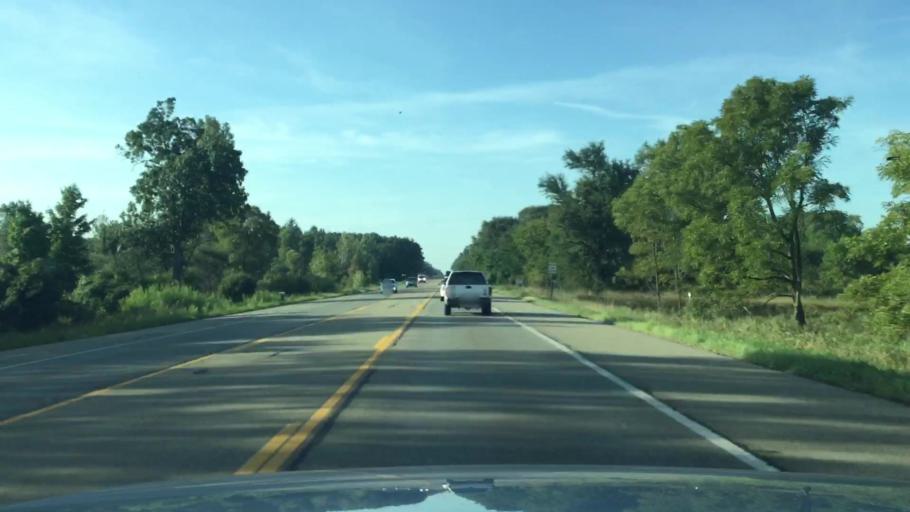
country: US
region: Michigan
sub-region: Jackson County
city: Vandercook Lake
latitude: 42.1749
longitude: -84.3647
